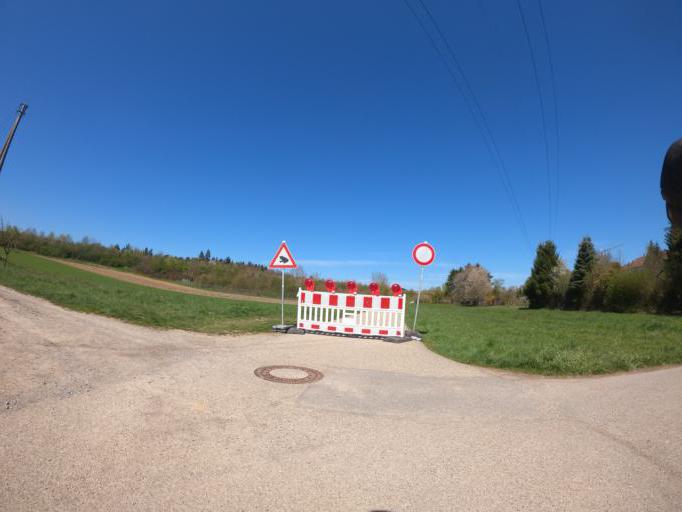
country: DE
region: Baden-Wuerttemberg
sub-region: Karlsruhe Region
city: Pforzheim
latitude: 48.9098
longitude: 8.7019
